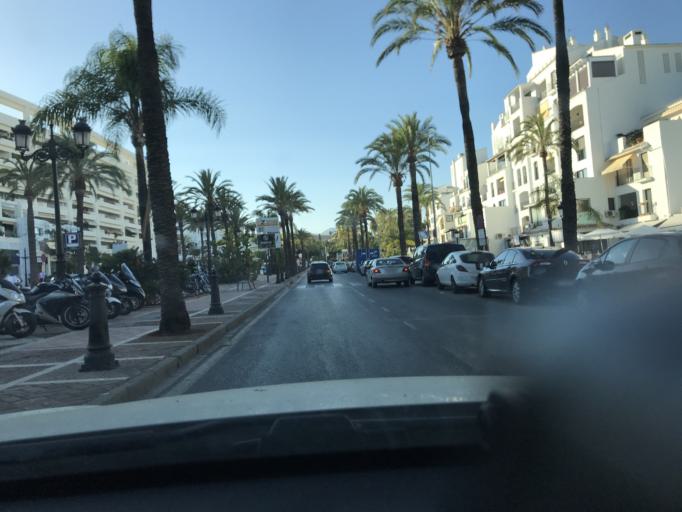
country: ES
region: Andalusia
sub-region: Provincia de Malaga
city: Marbella
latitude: 36.4868
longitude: -4.9557
